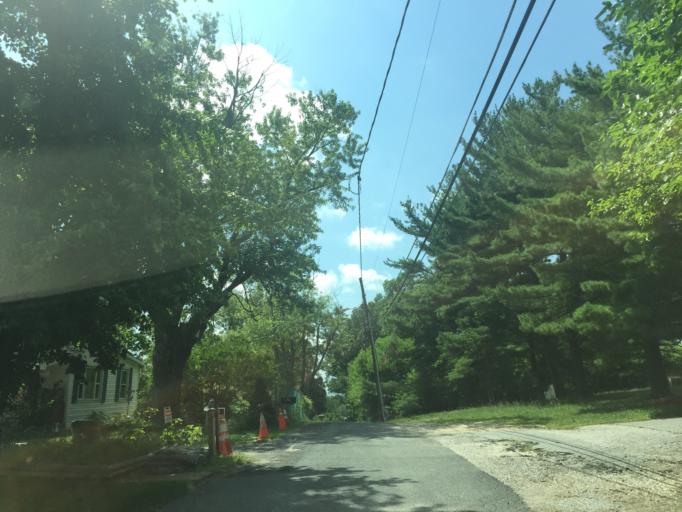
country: US
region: Maryland
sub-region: Baltimore County
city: Carney
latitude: 39.3923
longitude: -76.5190
